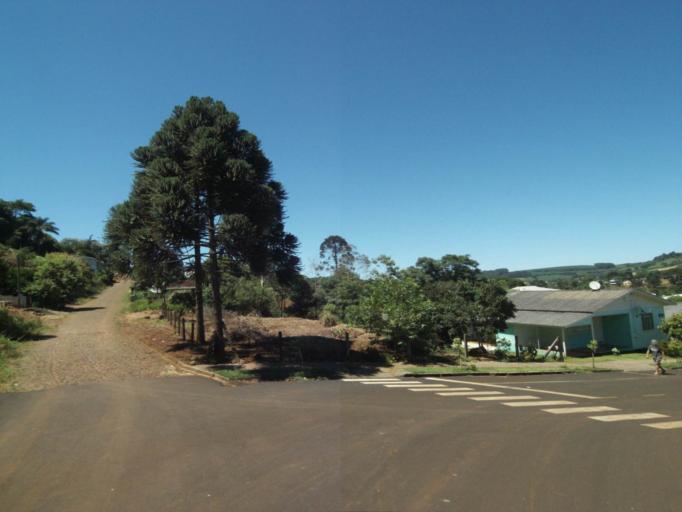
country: BR
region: Parana
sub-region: Pato Branco
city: Pato Branco
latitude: -26.2667
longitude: -52.7747
